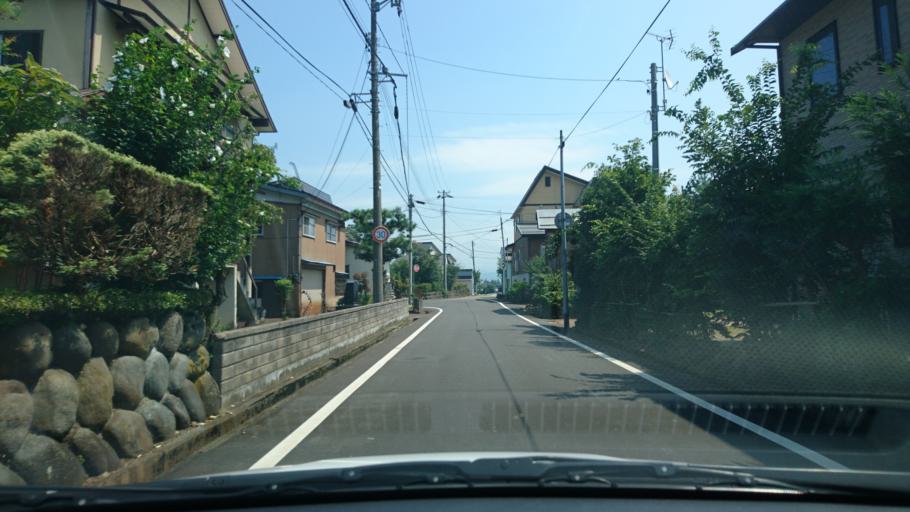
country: JP
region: Niigata
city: Arai
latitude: 37.0690
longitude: 138.2446
